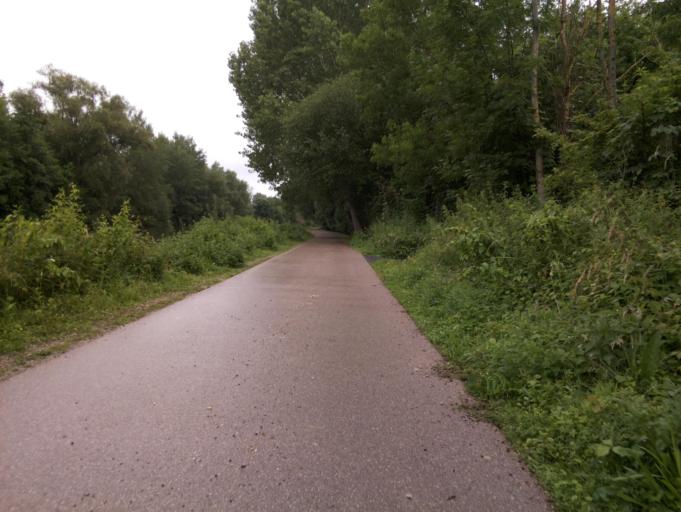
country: FR
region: Picardie
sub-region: Departement de la Somme
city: Ailly-sur-Somme
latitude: 49.9411
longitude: 2.1779
